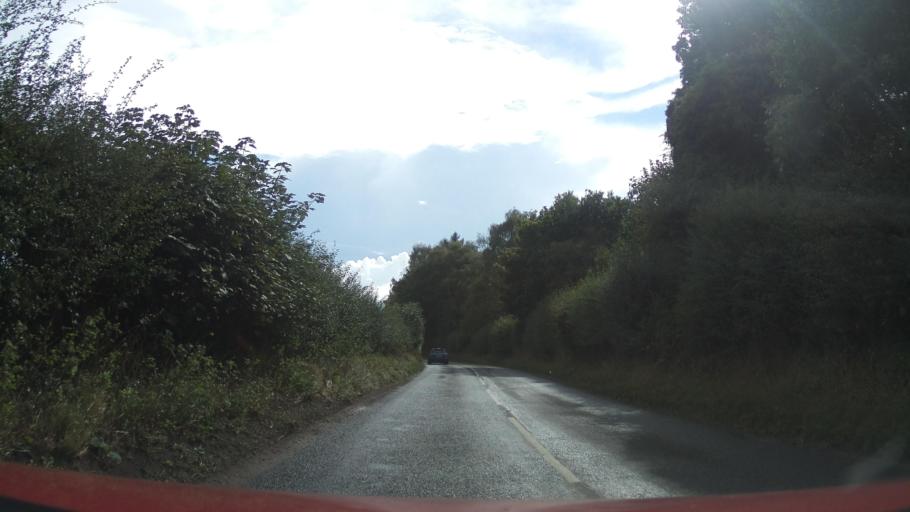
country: GB
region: England
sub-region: Shropshire
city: Shifnal
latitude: 52.6865
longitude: -2.3629
